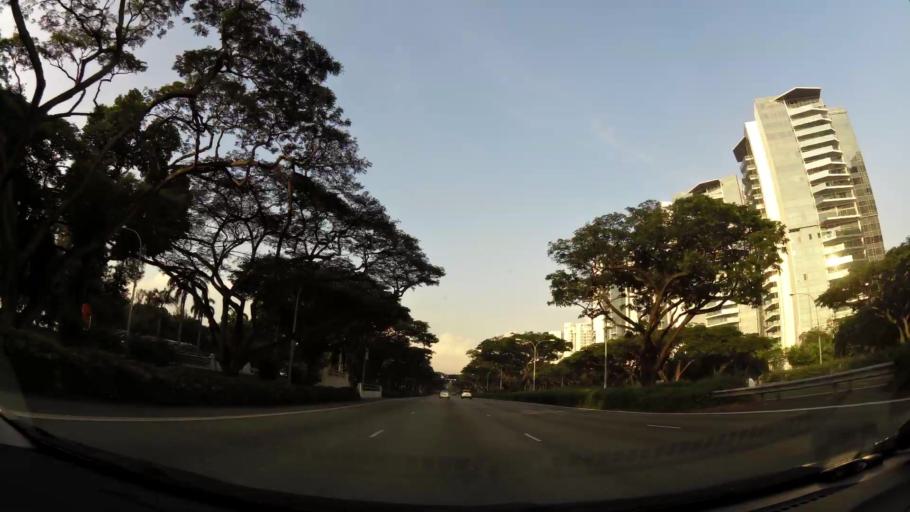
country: SG
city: Singapore
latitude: 1.2994
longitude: 103.9040
